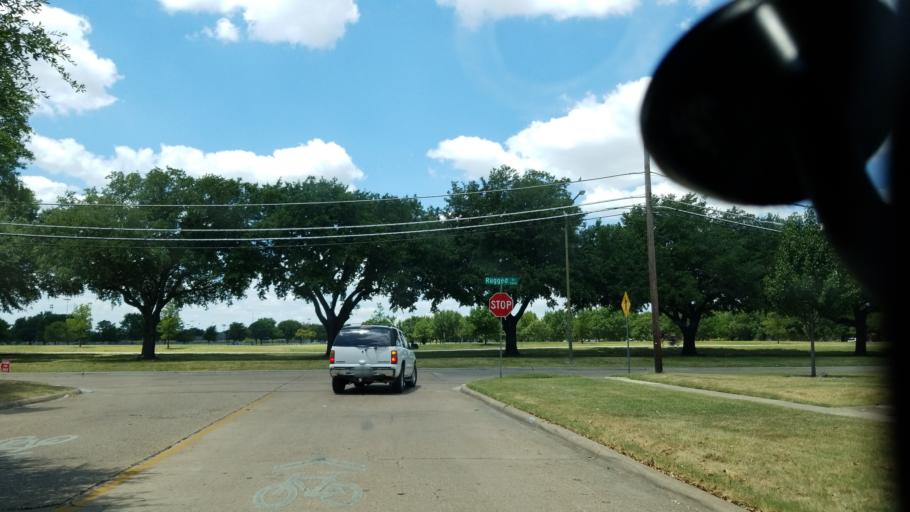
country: US
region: Texas
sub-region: Dallas County
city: Cockrell Hill
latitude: 32.7130
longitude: -96.8482
